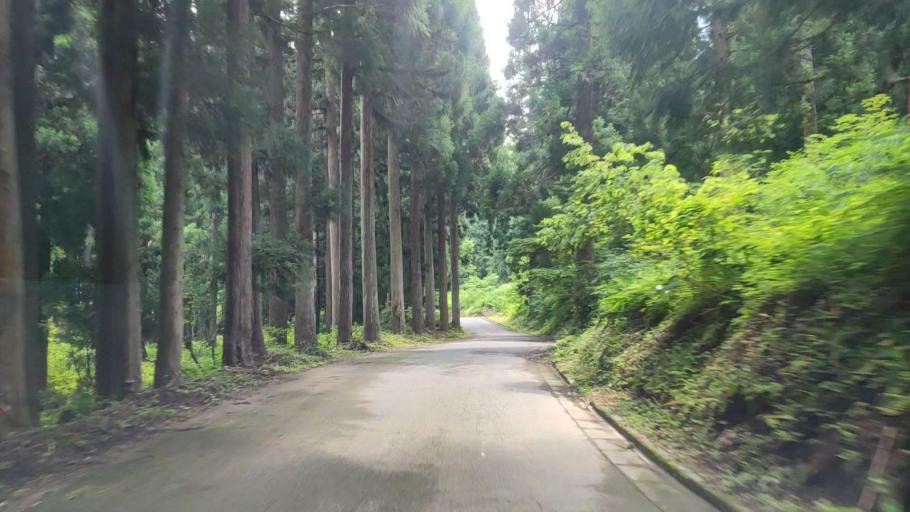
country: JP
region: Fukui
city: Ono
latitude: 35.8097
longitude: 136.4645
